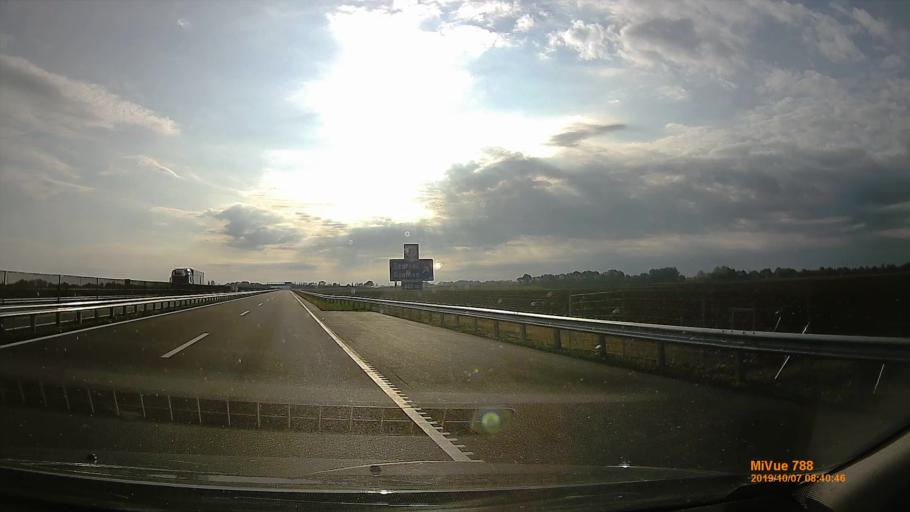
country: HU
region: Bekes
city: Bekesszentandras
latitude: 46.8224
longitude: 20.5035
